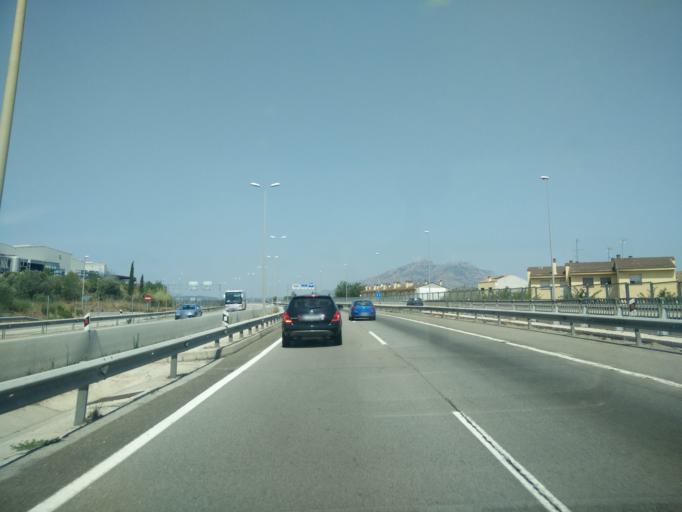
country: ES
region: Catalonia
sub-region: Provincia de Barcelona
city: Abrera
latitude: 41.5200
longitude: 1.8953
